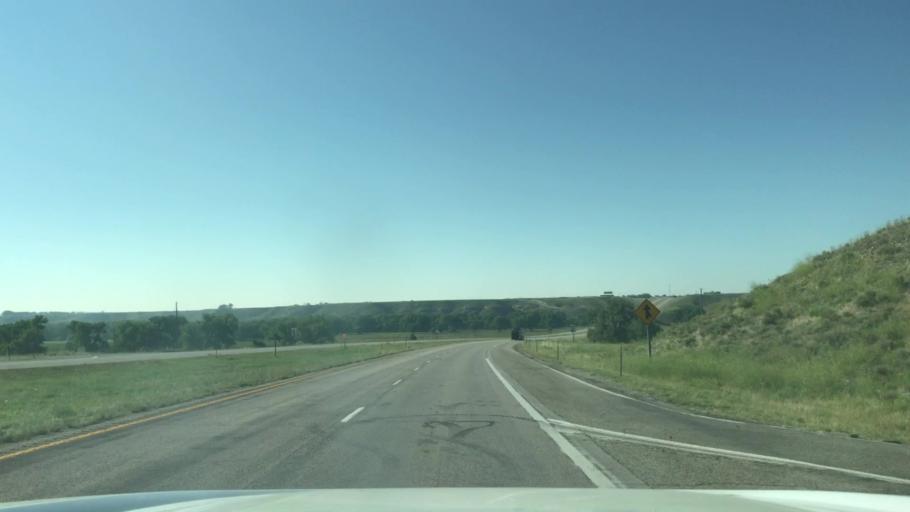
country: US
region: Wyoming
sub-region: Platte County
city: Wheatland
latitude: 42.1226
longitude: -104.9938
